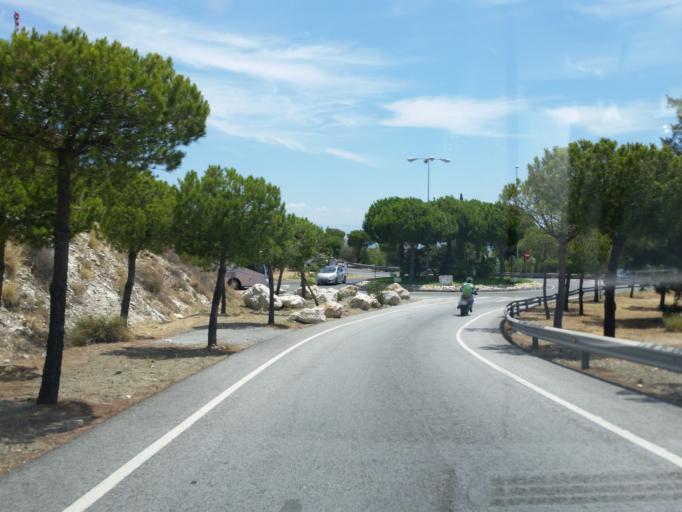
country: ES
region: Andalusia
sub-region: Provincia de Malaga
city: Benalmadena
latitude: 36.6067
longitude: -4.5435
